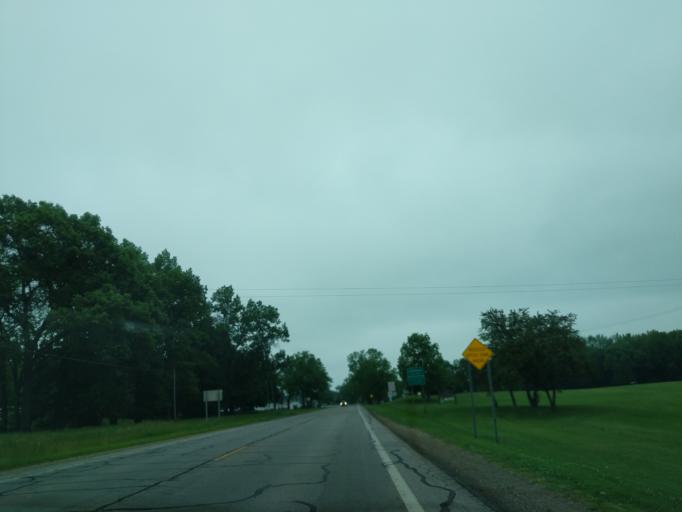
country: US
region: Michigan
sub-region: Hillsdale County
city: Litchfield
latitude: 42.0556
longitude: -84.7728
